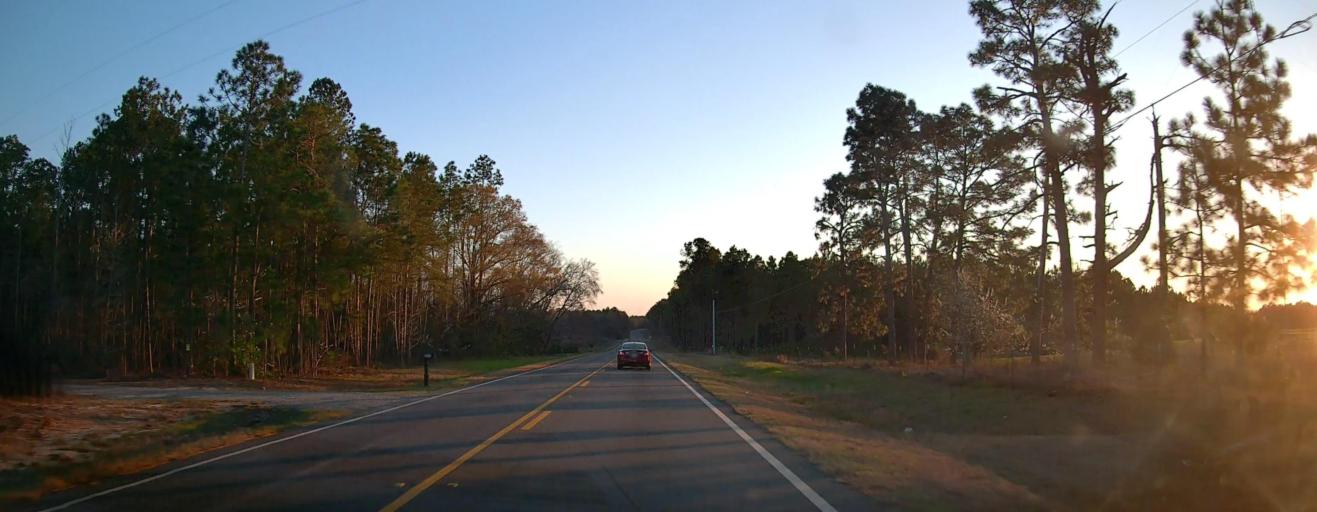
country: US
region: Georgia
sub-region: Dodge County
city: Chester
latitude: 32.3314
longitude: -83.0472
